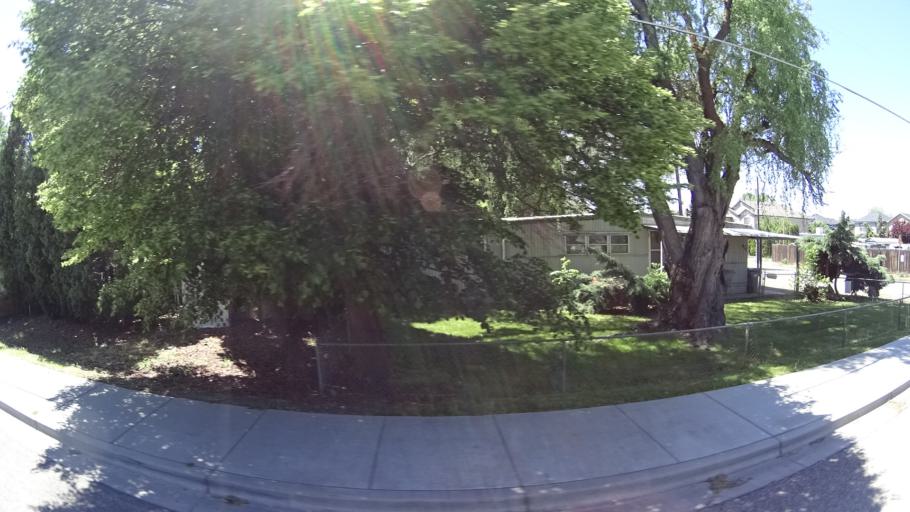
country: US
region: Idaho
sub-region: Ada County
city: Boise
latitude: 43.5861
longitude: -116.1778
